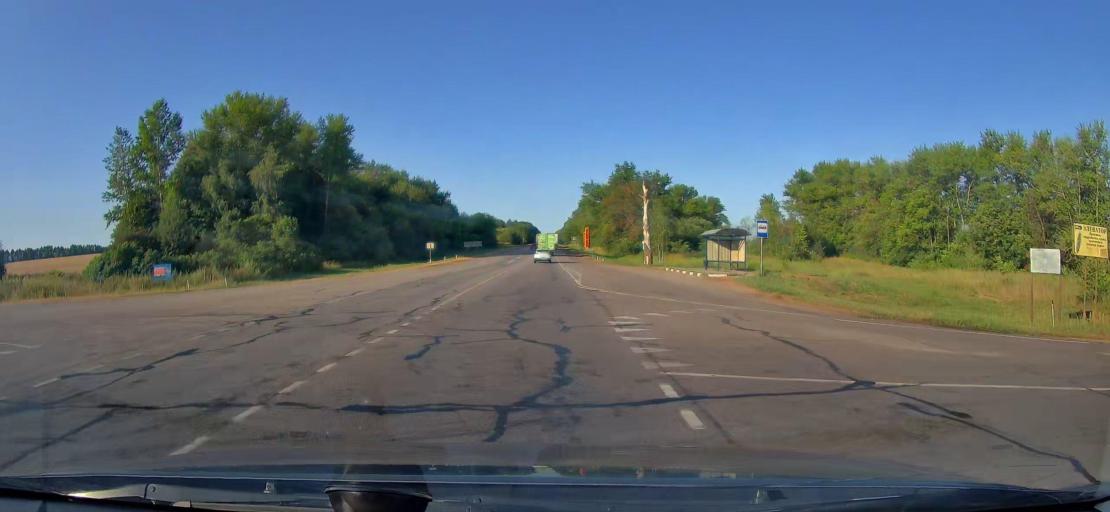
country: RU
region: Tula
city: Plavsk
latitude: 53.5864
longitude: 37.1510
